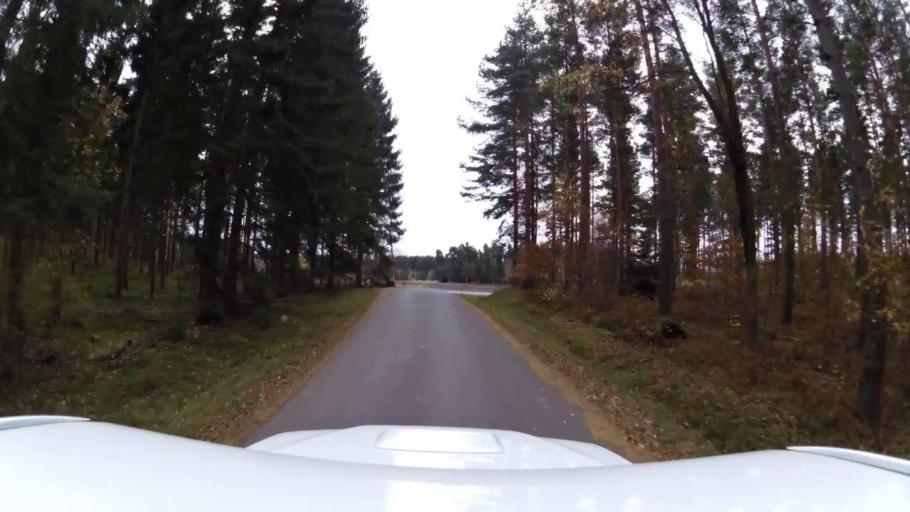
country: SE
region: OEstergoetland
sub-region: Linkopings Kommun
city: Linghem
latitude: 58.4026
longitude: 15.8448
